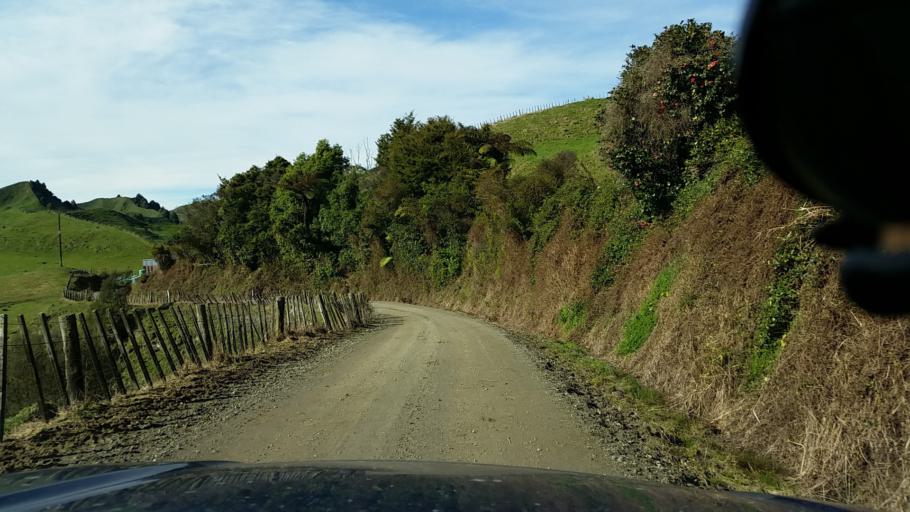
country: NZ
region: Taranaki
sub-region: New Plymouth District
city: Waitara
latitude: -39.0501
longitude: 174.7649
